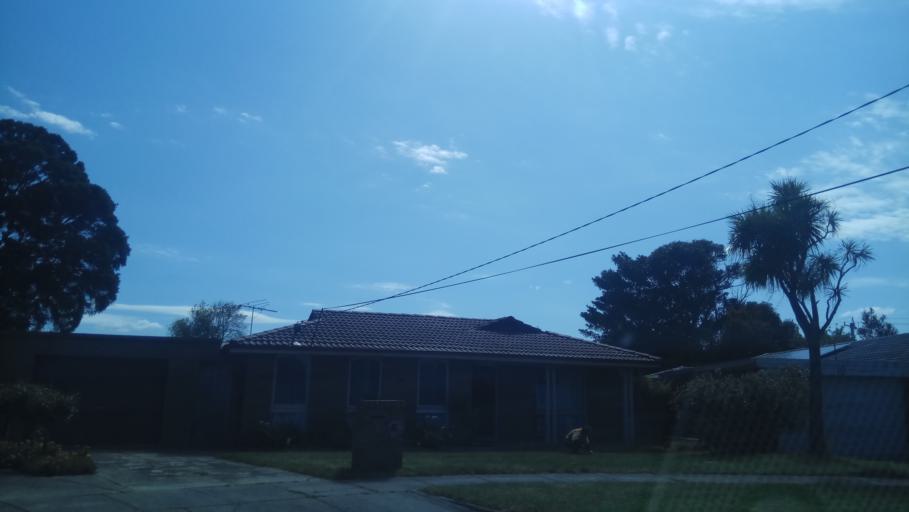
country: AU
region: Victoria
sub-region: Kingston
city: Clayton South
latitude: -37.9434
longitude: 145.1010
